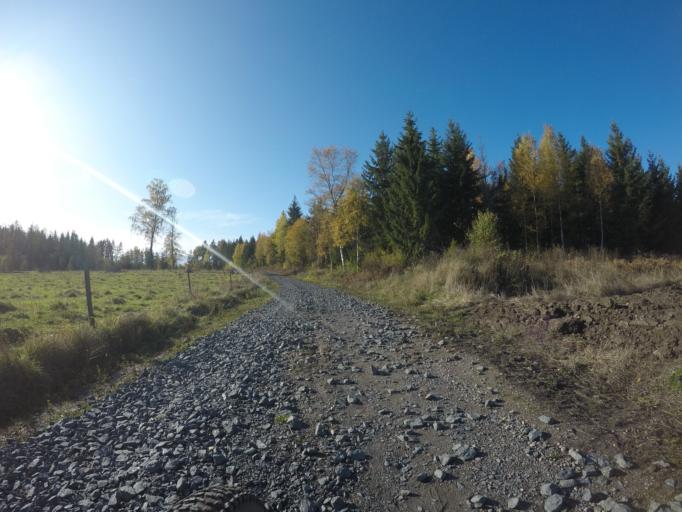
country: SE
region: Vaestmanland
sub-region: Kungsors Kommun
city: Kungsoer
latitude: 59.3233
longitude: 16.0915
